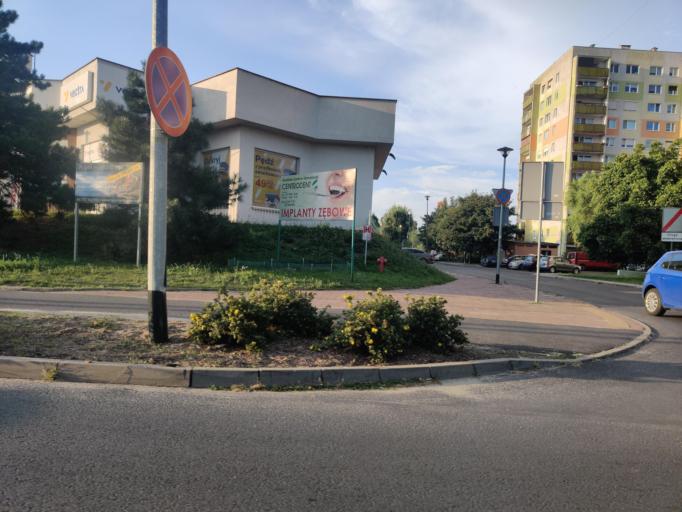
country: PL
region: Greater Poland Voivodeship
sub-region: Konin
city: Konin
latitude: 52.2326
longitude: 18.2533
